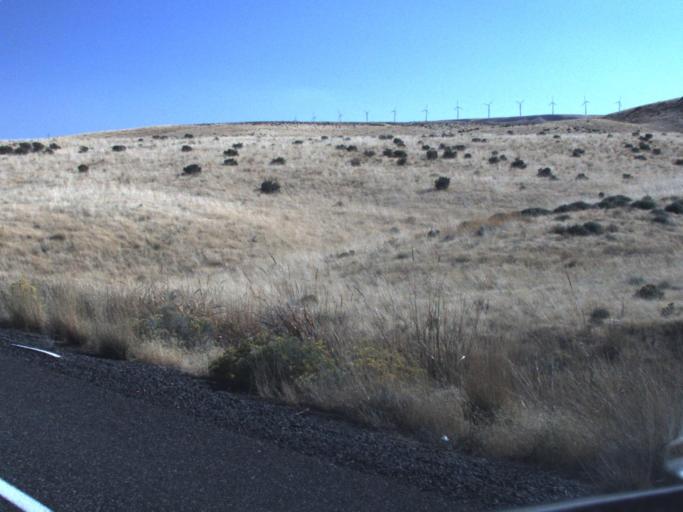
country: US
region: Washington
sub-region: Benton County
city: Highland
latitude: 46.1446
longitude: -119.1133
